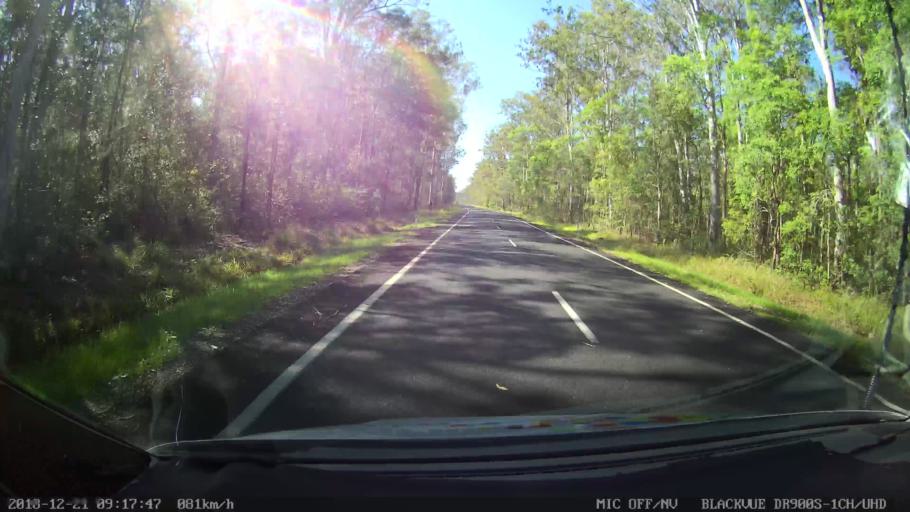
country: AU
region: New South Wales
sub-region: Clarence Valley
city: Maclean
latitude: -29.2964
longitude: 152.9919
